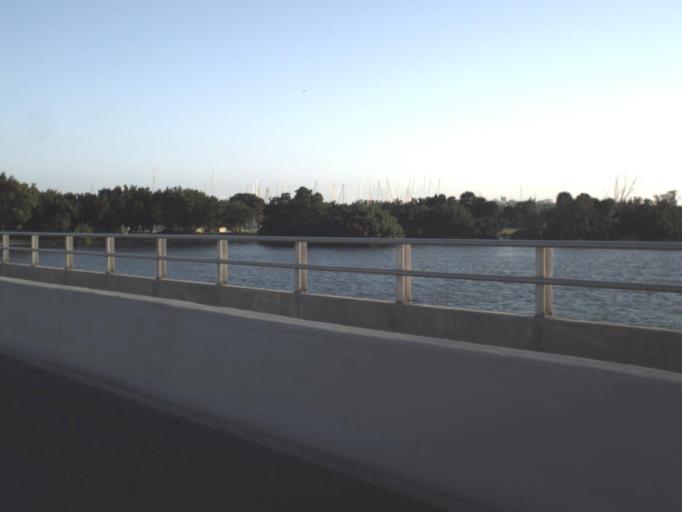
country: US
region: Florida
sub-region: Miami-Dade County
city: Key Biscayne
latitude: 25.7291
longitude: -80.1573
